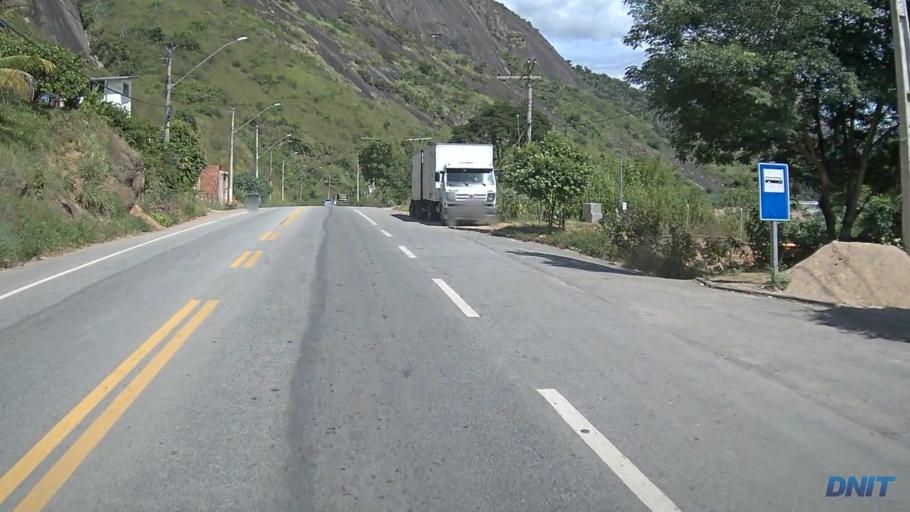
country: BR
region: Minas Gerais
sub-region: Timoteo
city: Timoteo
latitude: -19.5400
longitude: -42.6716
